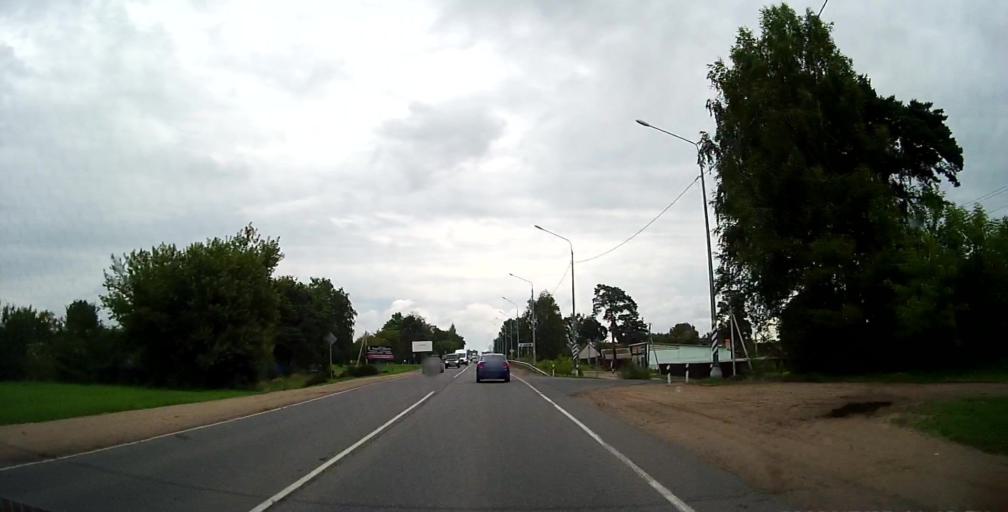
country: RU
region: Smolensk
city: Katyn'
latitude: 54.7838
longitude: 31.8346
